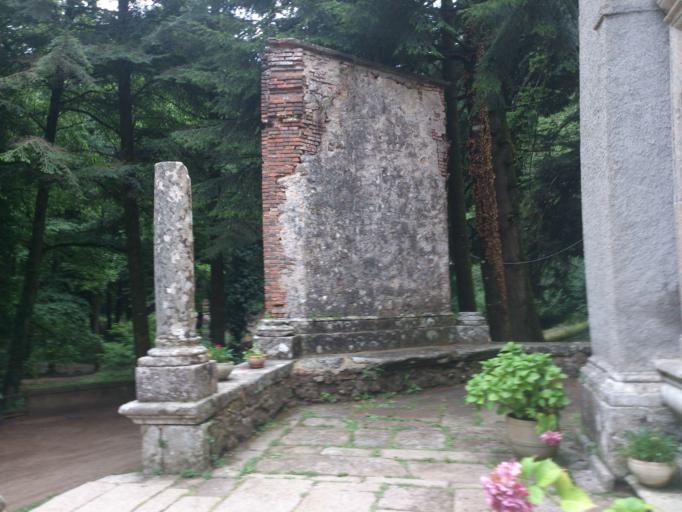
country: IT
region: Calabria
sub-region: Provincia di Vibo-Valentia
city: Serra San Bruno
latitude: 38.5541
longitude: 16.3121
